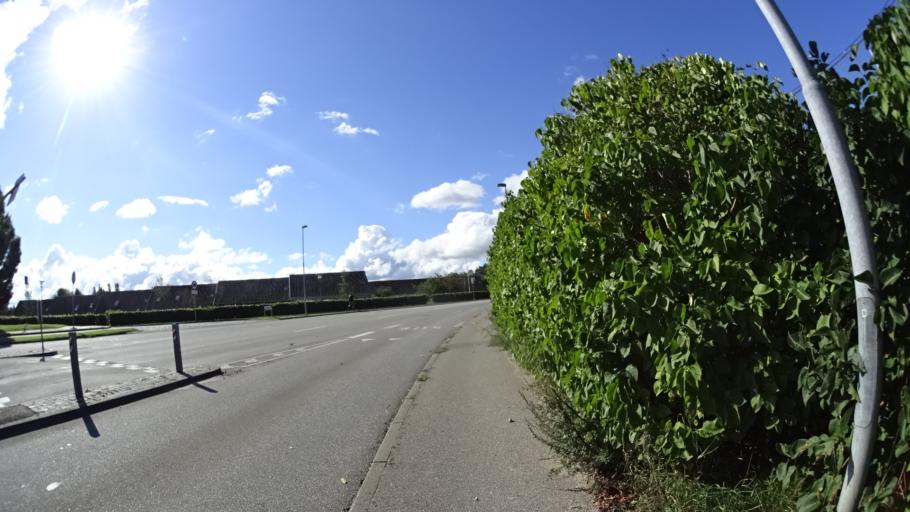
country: DK
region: Central Jutland
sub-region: Arhus Kommune
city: Marslet
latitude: 56.1133
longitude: 10.1713
